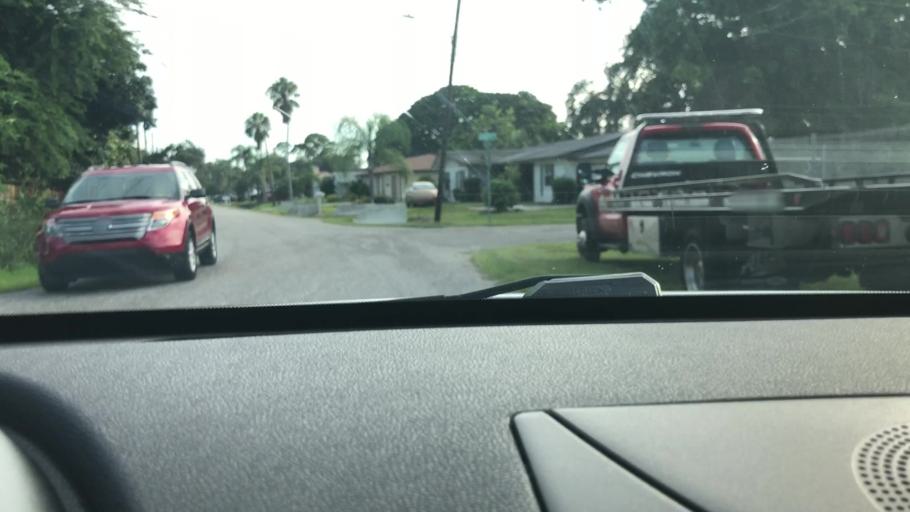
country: US
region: Florida
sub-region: Sarasota County
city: South Venice
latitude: 27.0484
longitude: -82.4064
